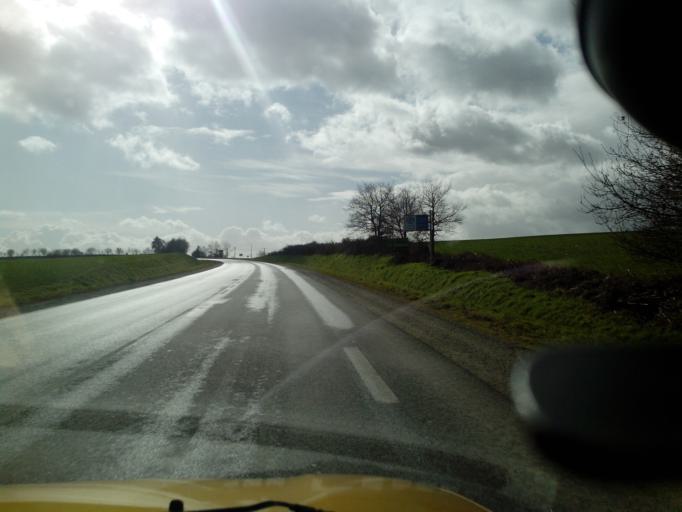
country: FR
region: Brittany
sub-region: Departement du Morbihan
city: Ploermel
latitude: 47.9535
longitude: -2.3945
